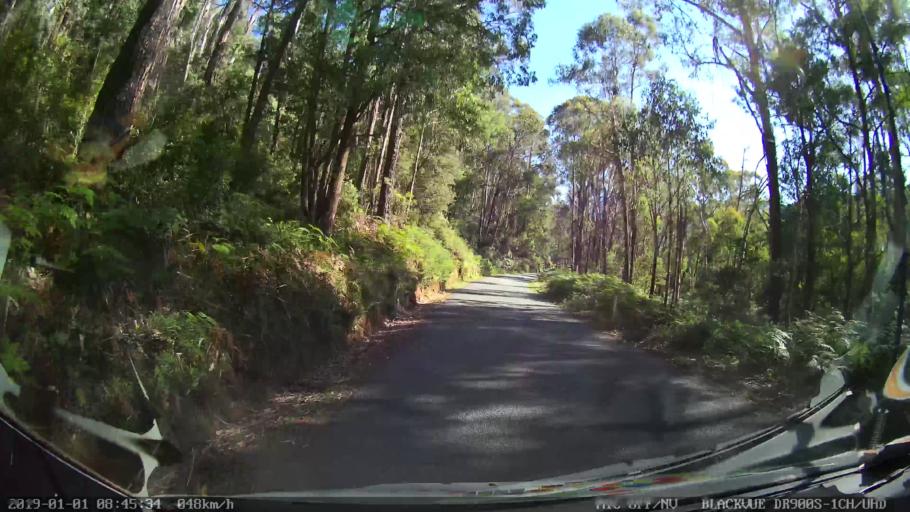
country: AU
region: New South Wales
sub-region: Snowy River
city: Jindabyne
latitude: -36.3048
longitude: 148.1891
